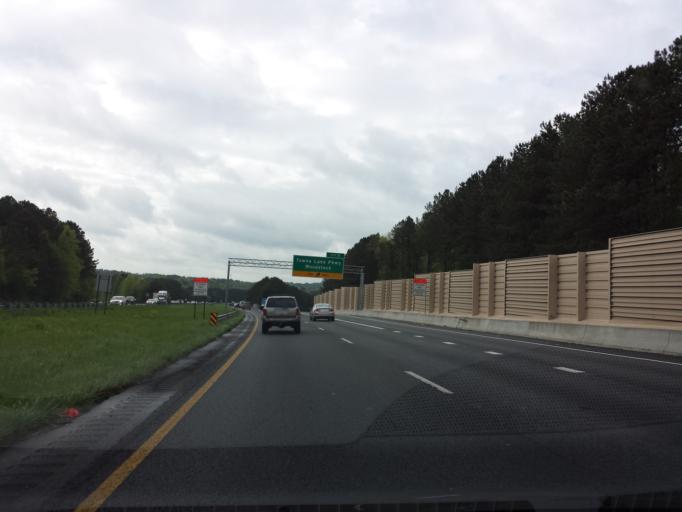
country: US
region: Georgia
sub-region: Cherokee County
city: Woodstock
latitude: 34.1082
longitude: -84.5336
